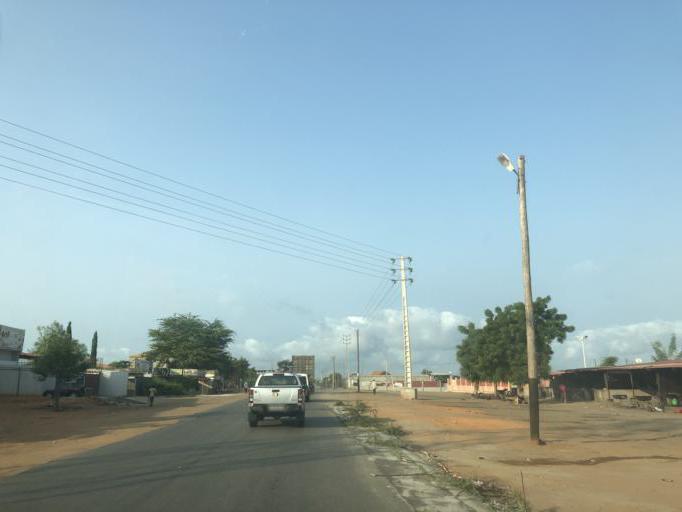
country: AO
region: Luanda
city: Luanda
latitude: -9.0602
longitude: 13.0461
